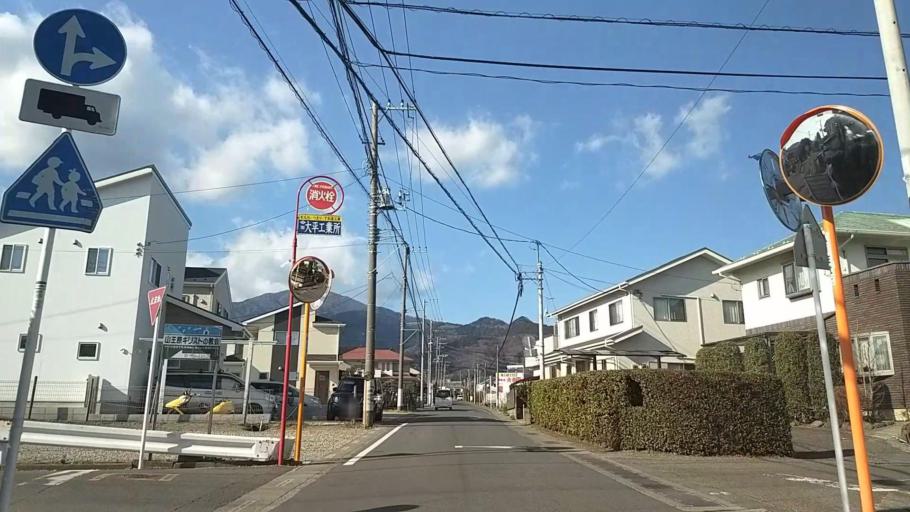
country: JP
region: Kanagawa
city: Isehara
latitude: 35.4091
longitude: 139.2911
